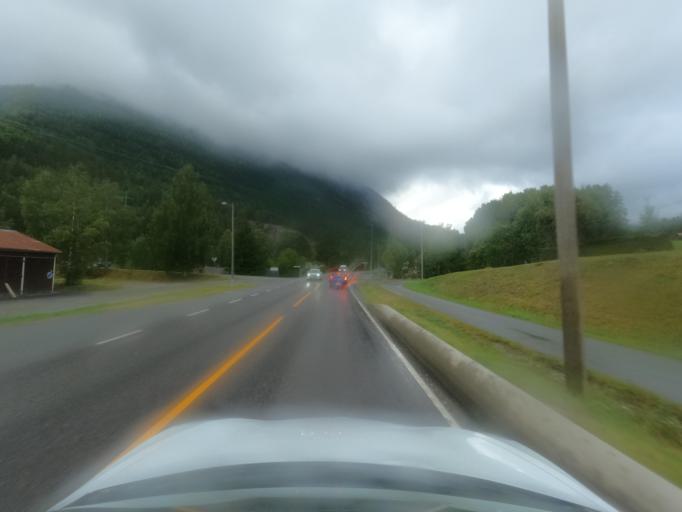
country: NO
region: Telemark
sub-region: Seljord
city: Seljord
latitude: 59.4970
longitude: 8.6372
